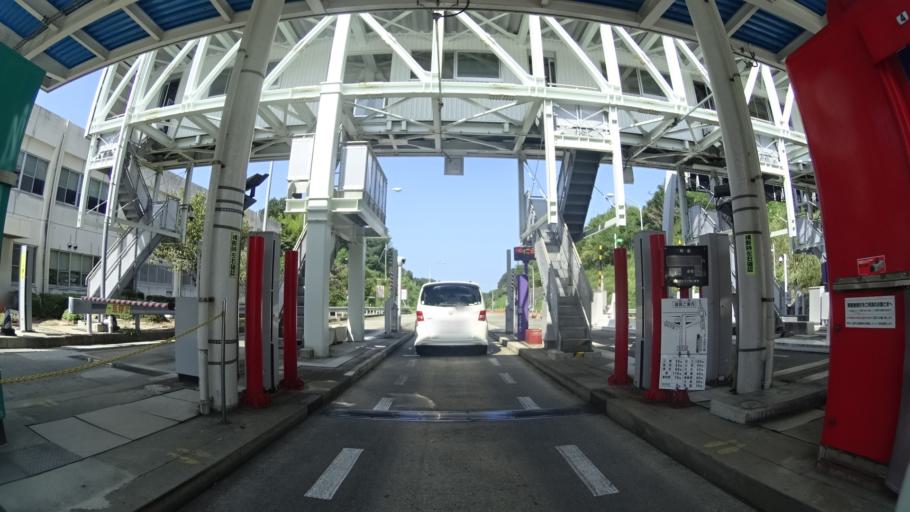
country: JP
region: Shimane
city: Hamada
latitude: 34.9091
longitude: 132.1138
